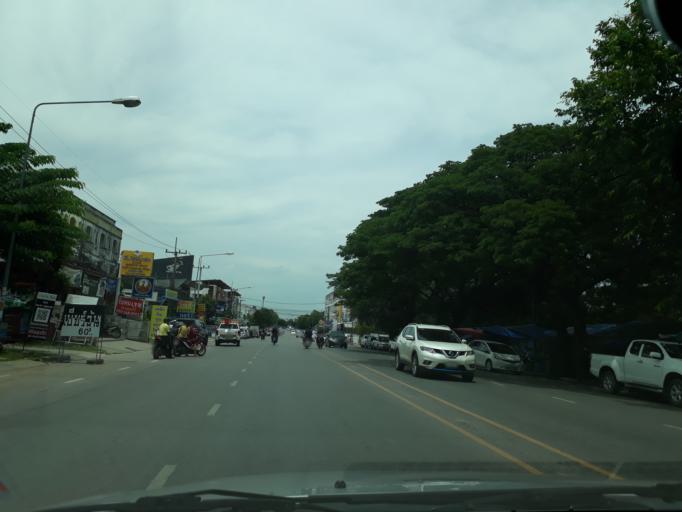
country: TH
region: Khon Kaen
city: Khon Kaen
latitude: 16.4340
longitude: 102.8615
